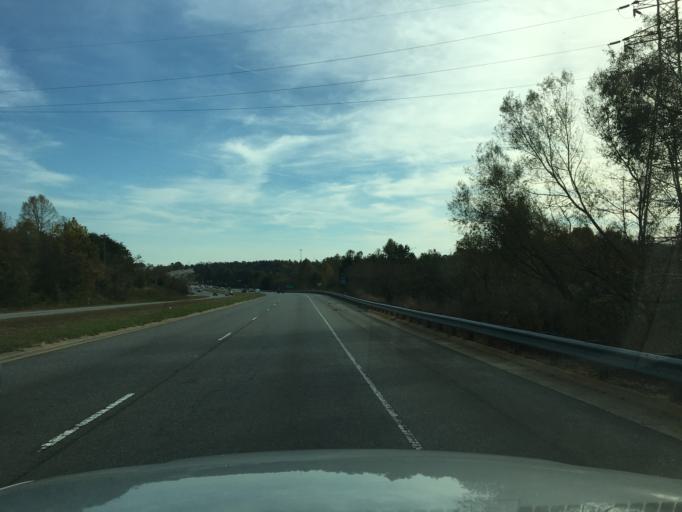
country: US
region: North Carolina
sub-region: Catawba County
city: Hickory
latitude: 35.7133
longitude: -81.2951
